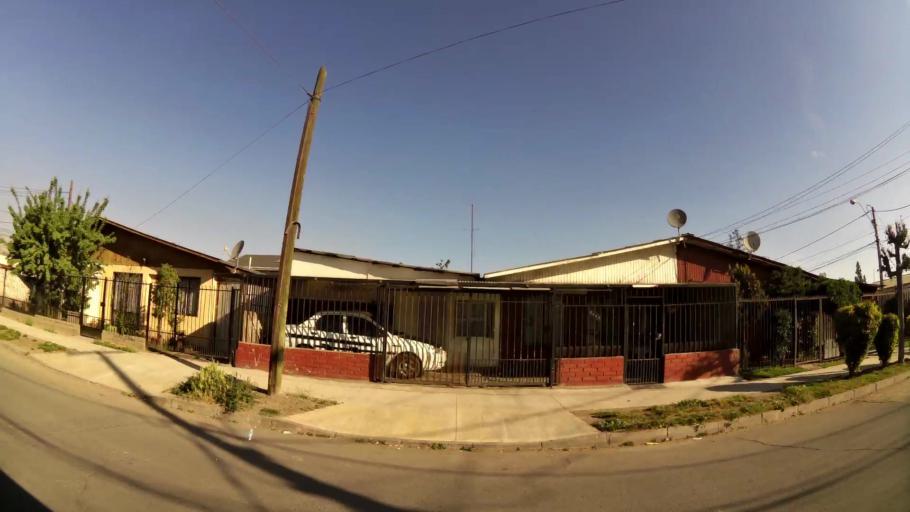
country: CL
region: Santiago Metropolitan
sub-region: Provincia de Santiago
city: La Pintana
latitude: -33.5548
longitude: -70.6262
